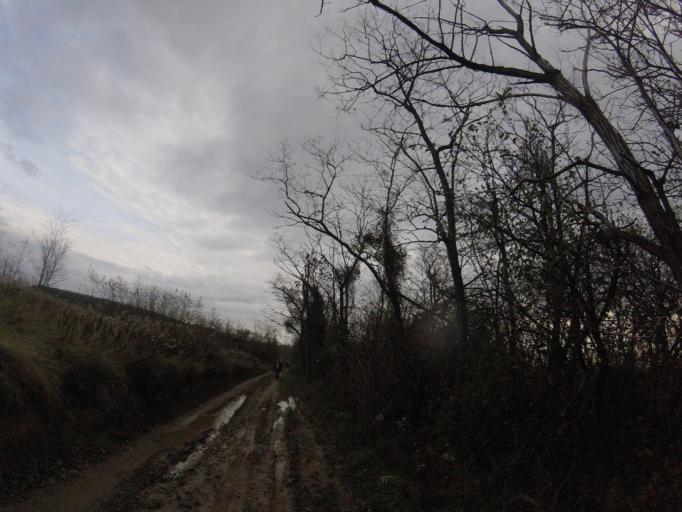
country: HU
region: Tolna
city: Szekszard
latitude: 46.3224
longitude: 18.6706
